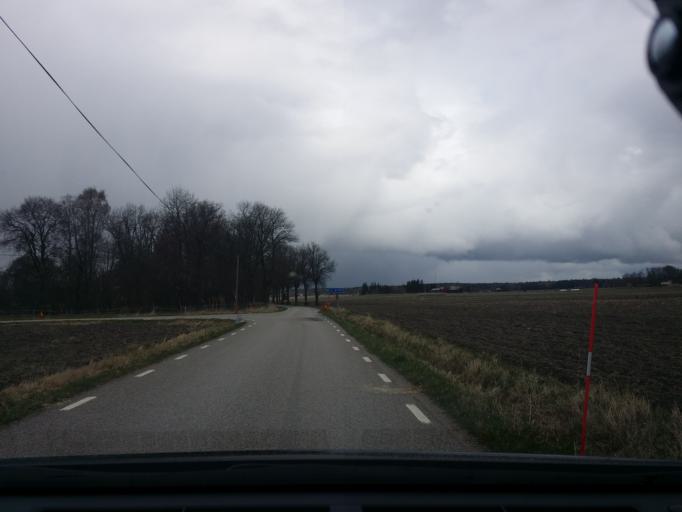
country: SE
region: Uppsala
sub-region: Enkopings Kommun
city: Enkoping
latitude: 59.6757
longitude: 17.0246
